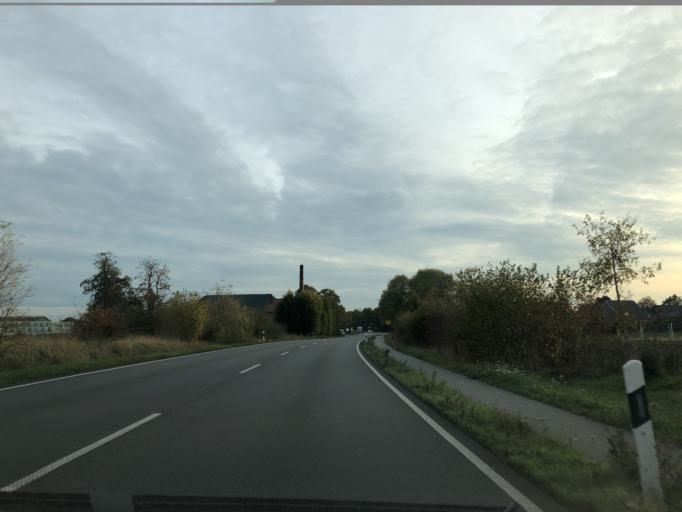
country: DE
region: Lower Saxony
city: Lehe
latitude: 53.0316
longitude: 7.3248
